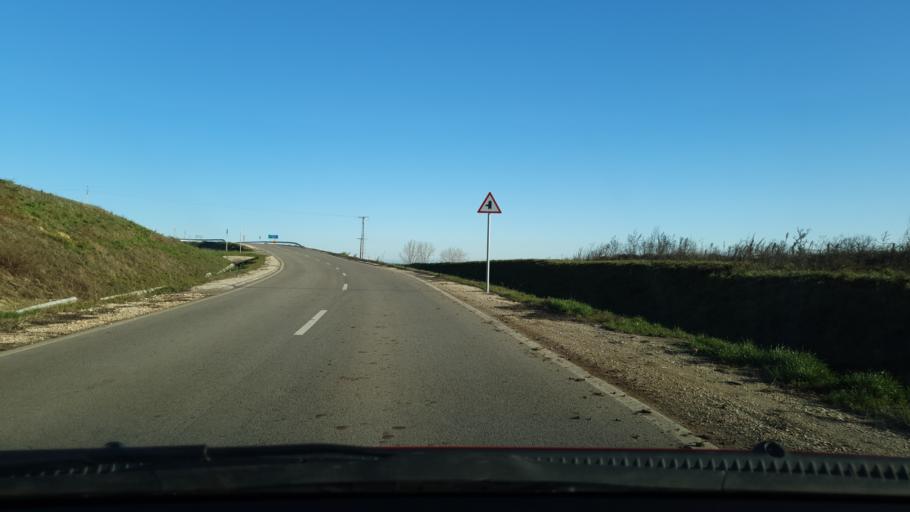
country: HU
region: Pest
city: Cegledbercel
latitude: 47.2193
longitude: 19.6921
